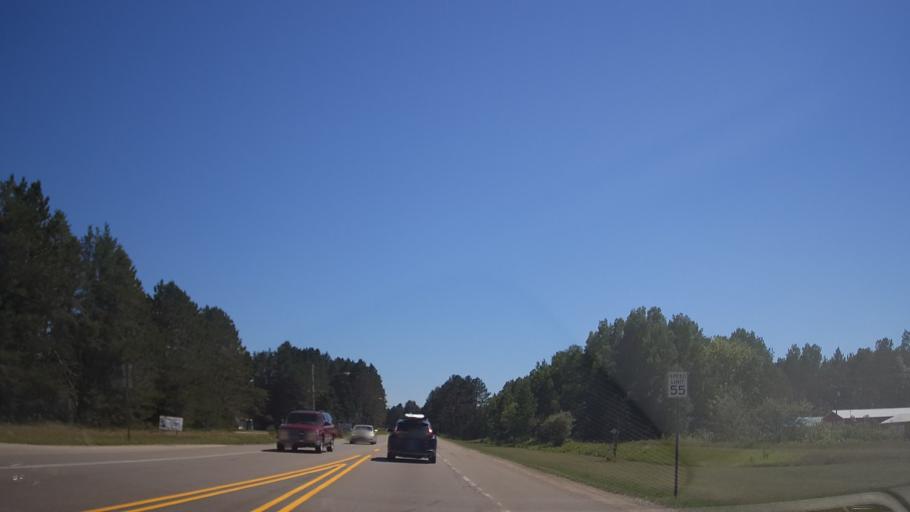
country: US
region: Michigan
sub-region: Cheboygan County
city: Indian River
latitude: 45.5504
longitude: -84.7844
